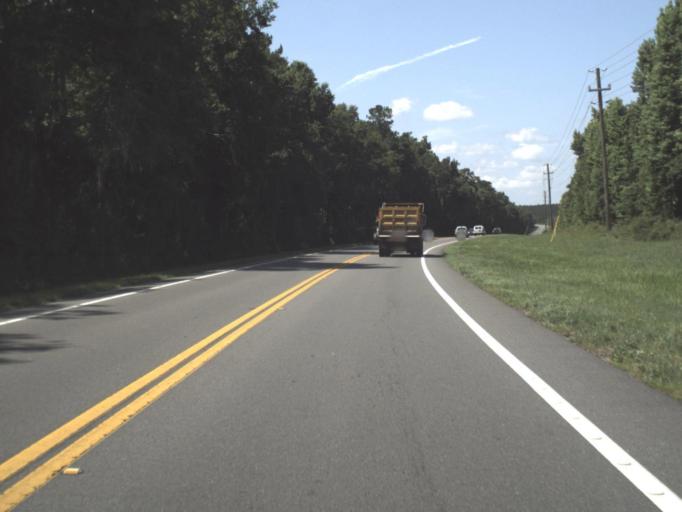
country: US
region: Florida
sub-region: Levy County
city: Williston
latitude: 29.4939
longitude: -82.4071
